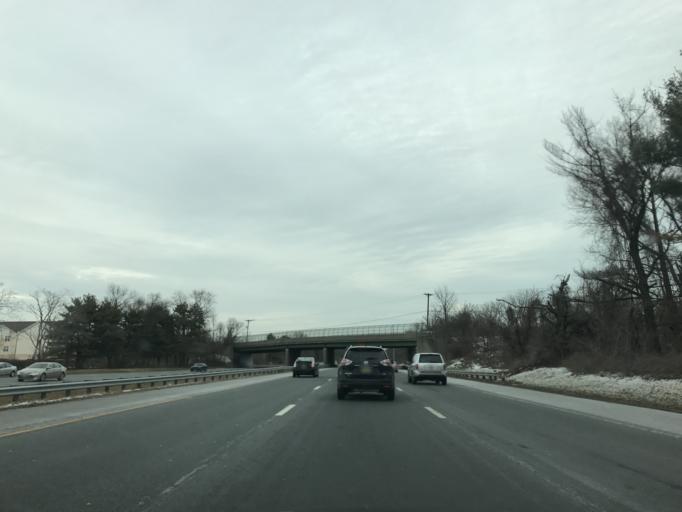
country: US
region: New Jersey
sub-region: Burlington County
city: Ramblewood
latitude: 39.9390
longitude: -74.9567
